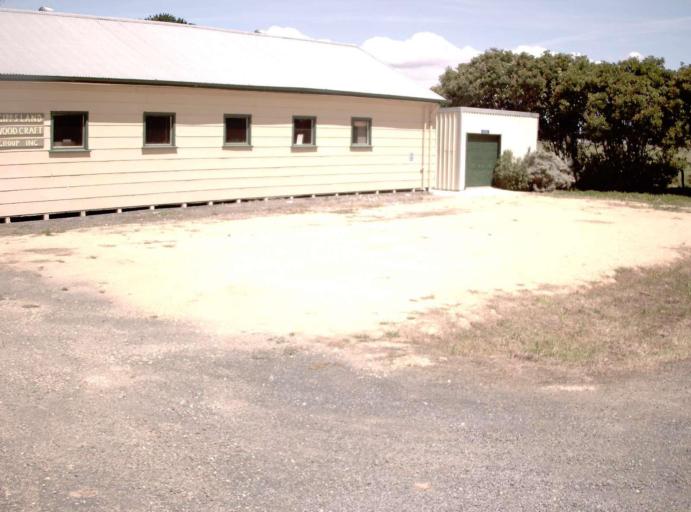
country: AU
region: Victoria
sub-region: Wellington
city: Heyfield
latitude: -38.0646
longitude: 146.8720
